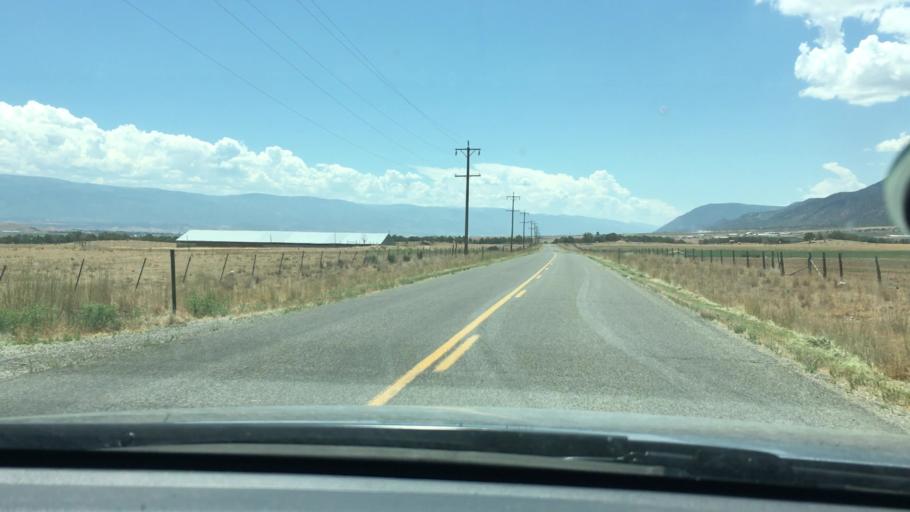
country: US
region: Utah
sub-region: Sanpete County
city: Fountain Green
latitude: 39.5987
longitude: -111.6434
